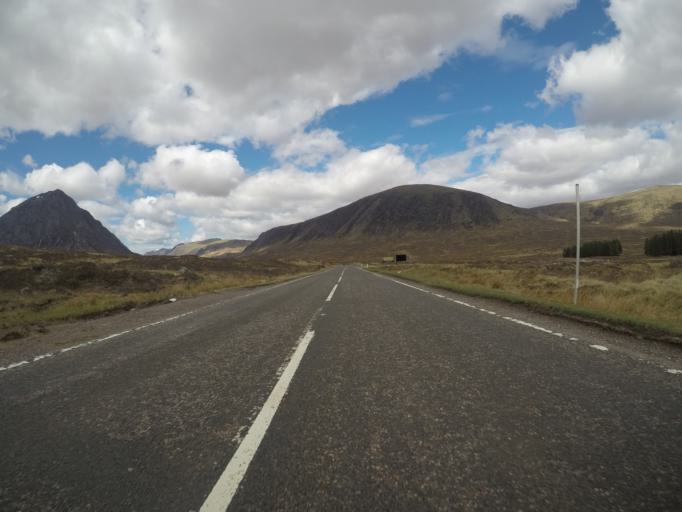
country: GB
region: Scotland
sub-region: Highland
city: Spean Bridge
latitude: 56.6480
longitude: -4.8443
